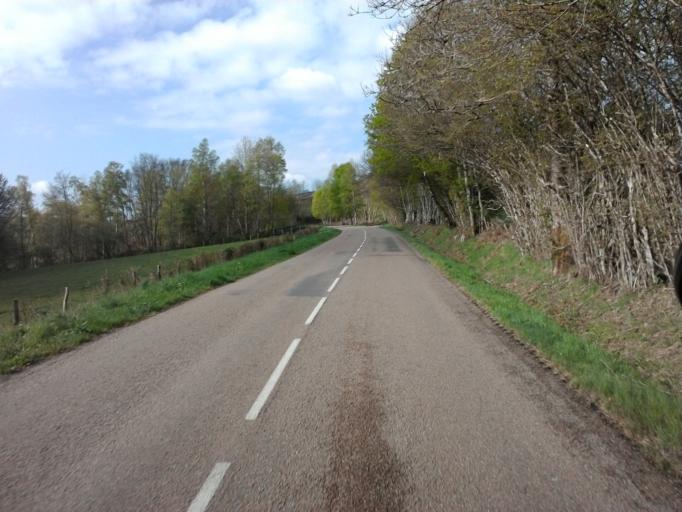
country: FR
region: Bourgogne
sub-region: Departement de la Nievre
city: Chateau-Chinon(Ville)
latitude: 47.2208
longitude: 4.0361
